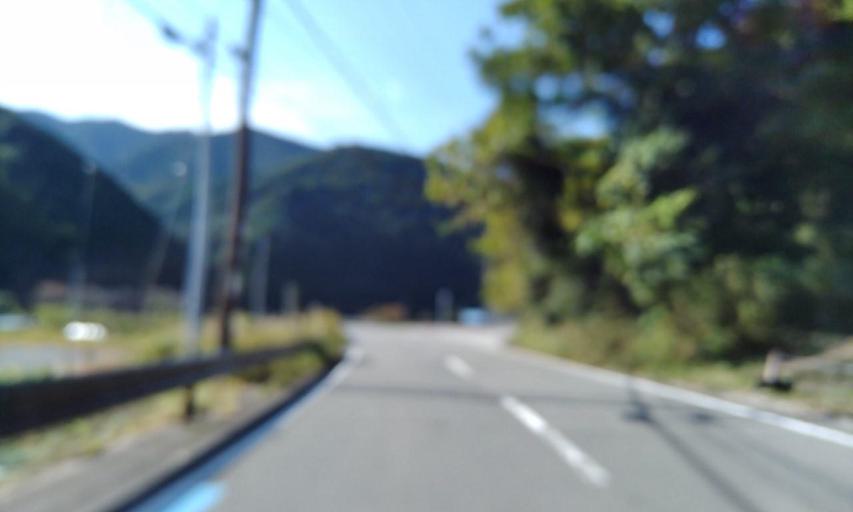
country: JP
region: Wakayama
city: Kainan
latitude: 34.0526
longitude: 135.3282
